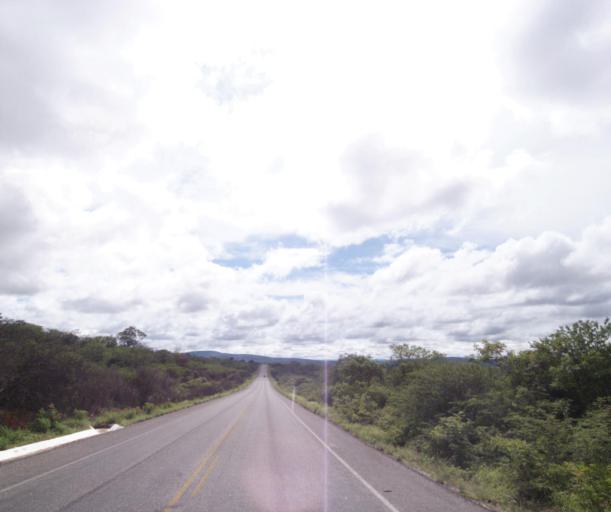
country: BR
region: Bahia
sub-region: Brumado
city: Brumado
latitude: -14.2366
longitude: -41.6992
